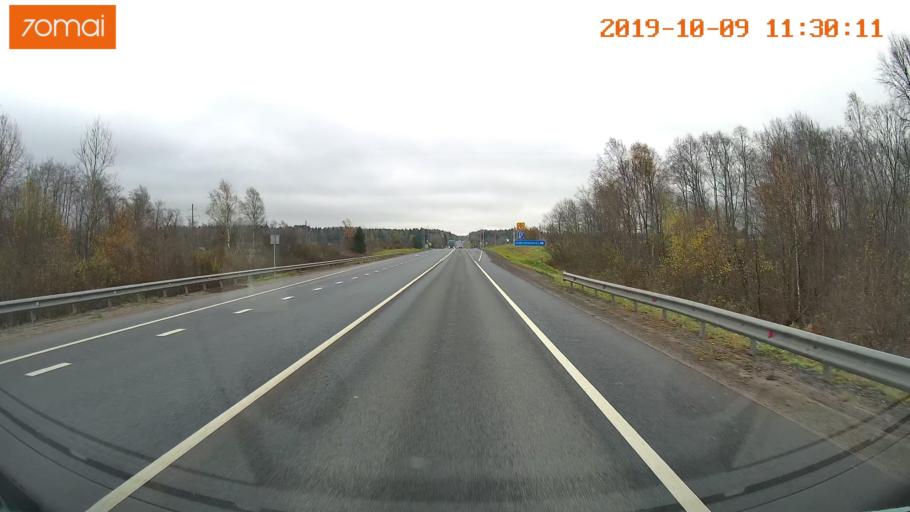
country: RU
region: Vologda
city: Vologda
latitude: 59.0560
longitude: 40.0695
